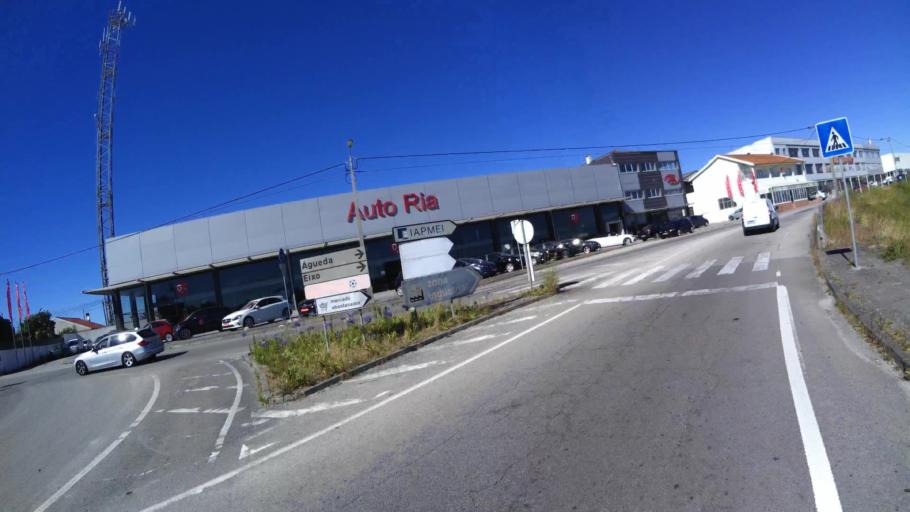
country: PT
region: Aveiro
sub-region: Aveiro
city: Aveiro
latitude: 40.6531
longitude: -8.6164
